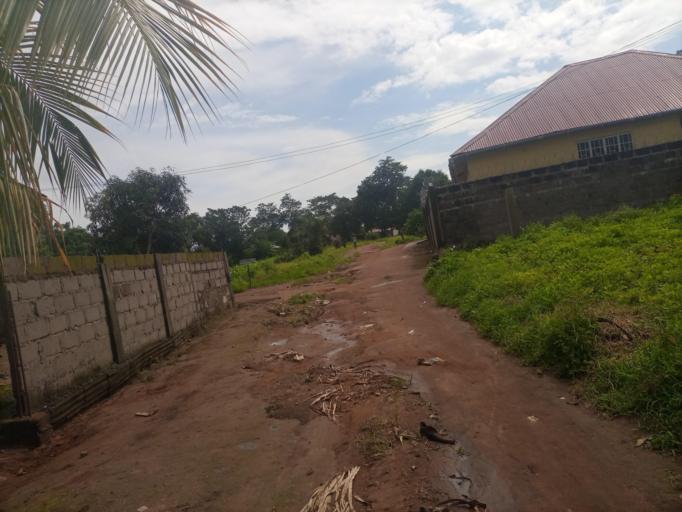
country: SL
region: Northern Province
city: Sawkta
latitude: 8.6354
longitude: -13.2091
